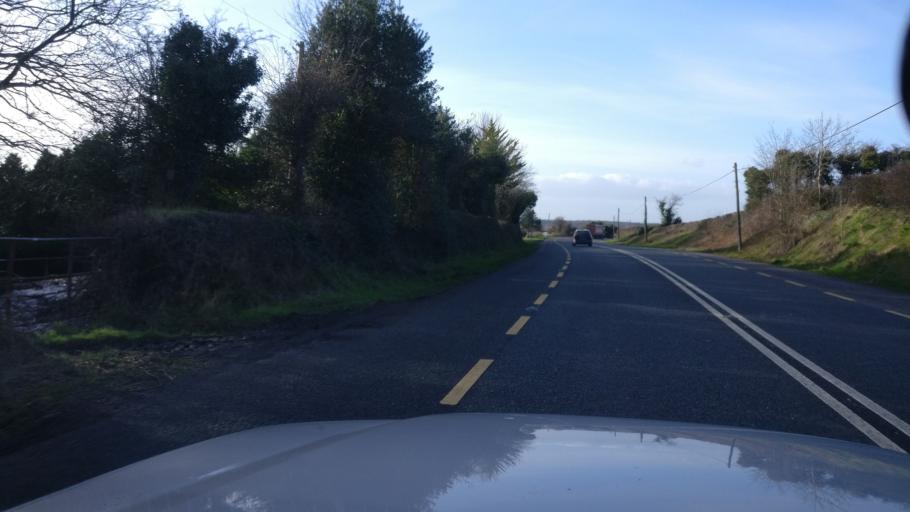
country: IE
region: Leinster
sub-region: Uibh Fhaili
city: Tullamore
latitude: 53.2174
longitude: -7.4660
